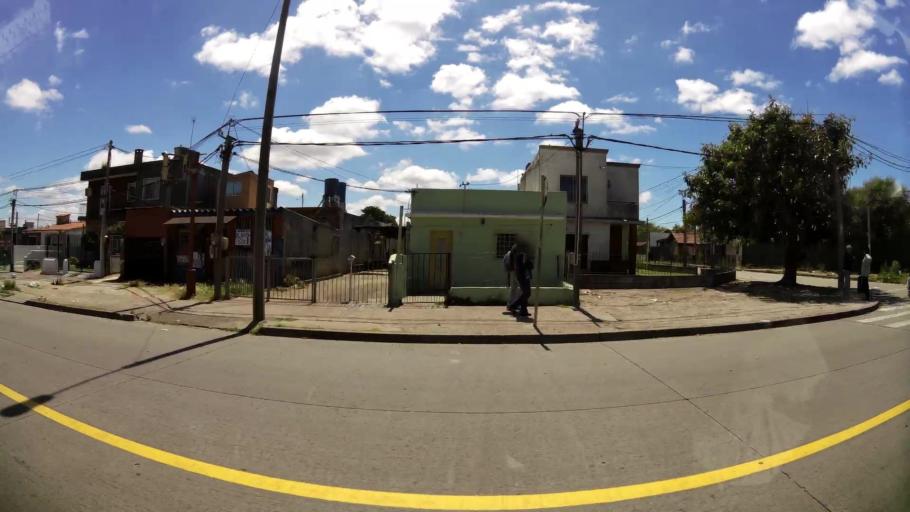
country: UY
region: Canelones
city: Paso de Carrasco
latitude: -34.8696
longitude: -56.1183
